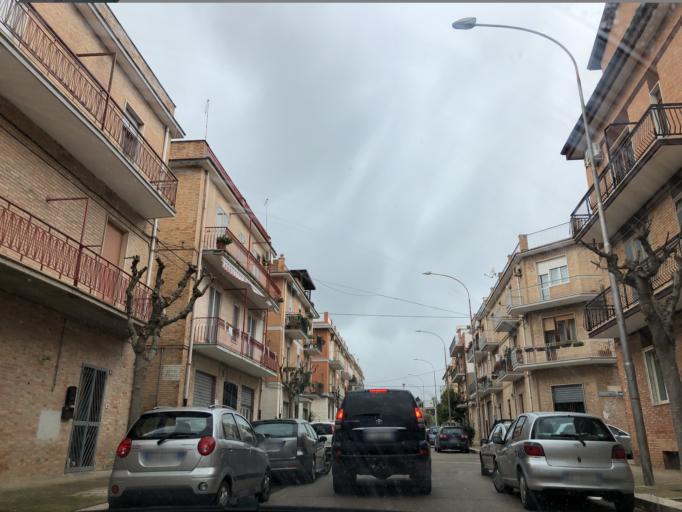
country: IT
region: Apulia
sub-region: Provincia di Foggia
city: Lucera
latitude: 41.5080
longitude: 15.3260
